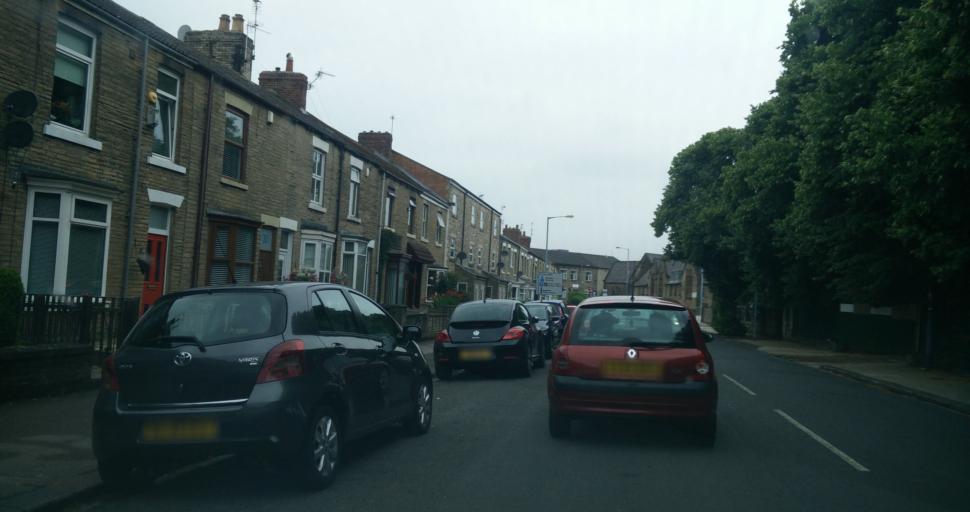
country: GB
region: England
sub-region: County Durham
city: Bishop Auckland
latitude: 54.6605
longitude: -1.6727
